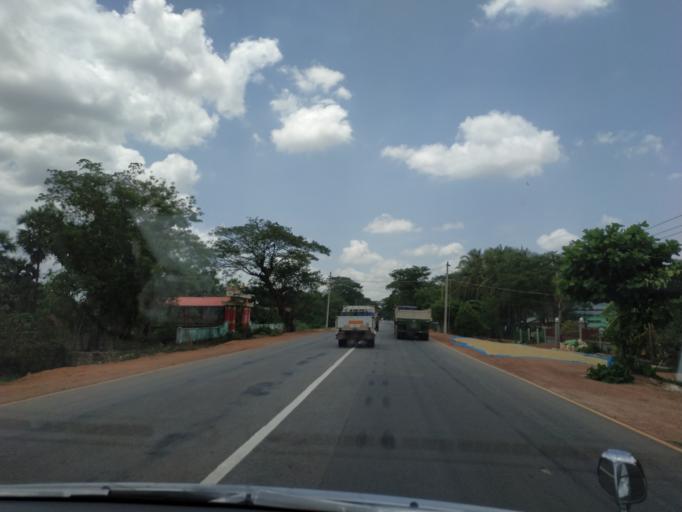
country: MM
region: Bago
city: Bago
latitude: 17.4673
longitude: 96.5798
